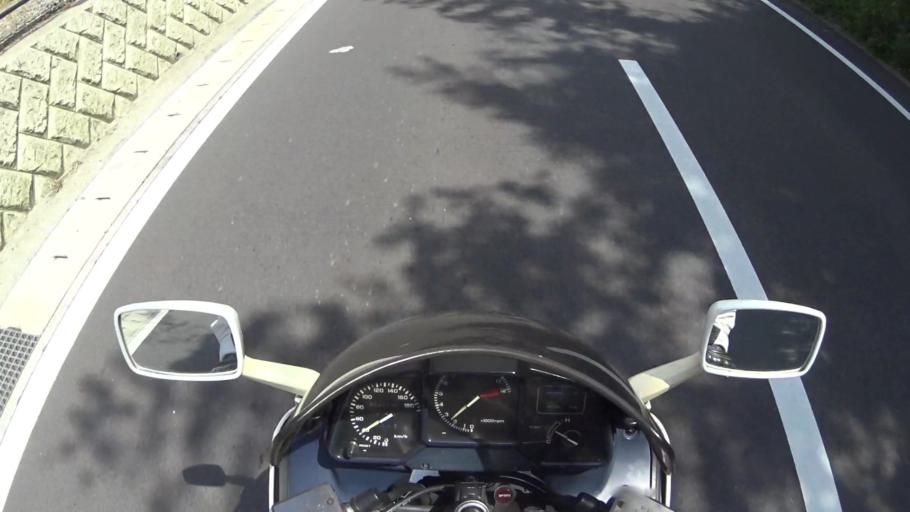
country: JP
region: Kyoto
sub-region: Kyoto-shi
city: Kamigyo-ku
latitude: 35.0910
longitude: 135.7654
